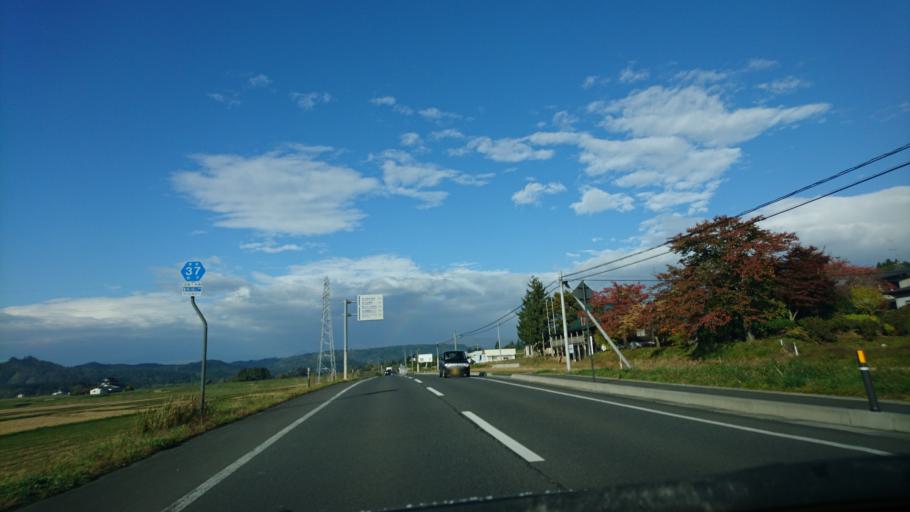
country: JP
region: Iwate
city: Ichinoseki
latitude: 39.0155
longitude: 141.1082
